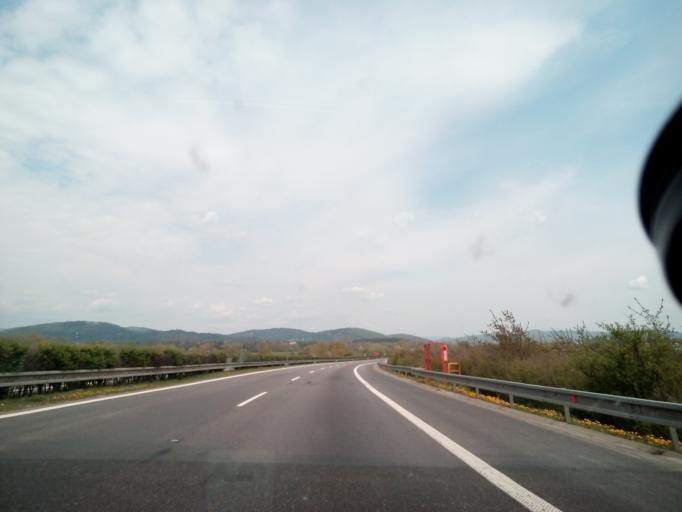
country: SK
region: Nitriansky
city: Ilava
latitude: 49.0383
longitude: 18.2739
